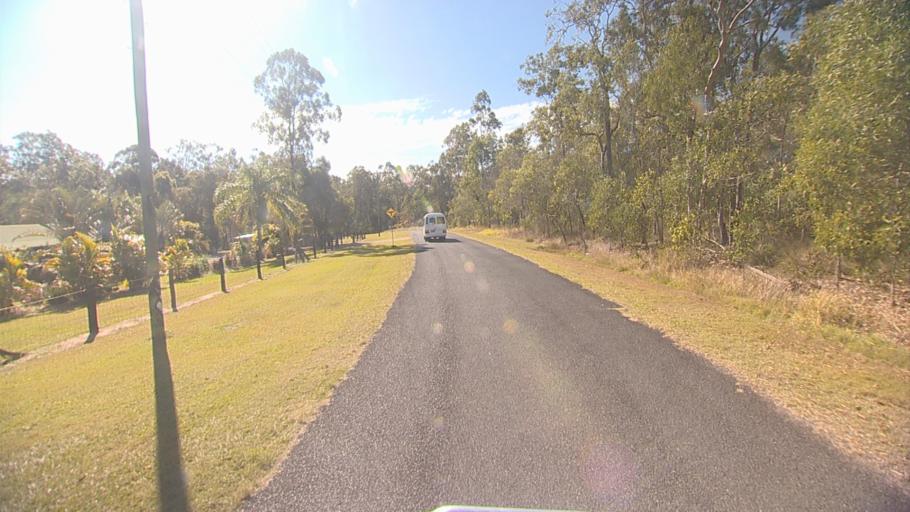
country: AU
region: Queensland
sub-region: Ipswich
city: Springfield Lakes
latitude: -27.7119
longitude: 152.9568
